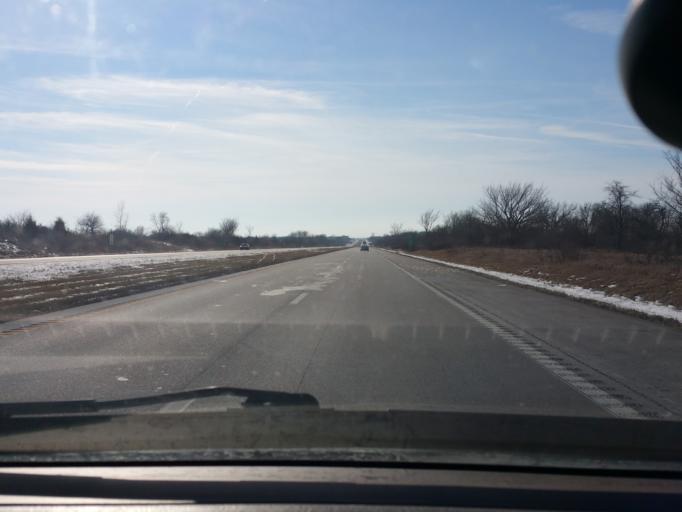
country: US
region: Missouri
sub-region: Clinton County
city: Cameron
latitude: 39.8314
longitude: -94.1868
